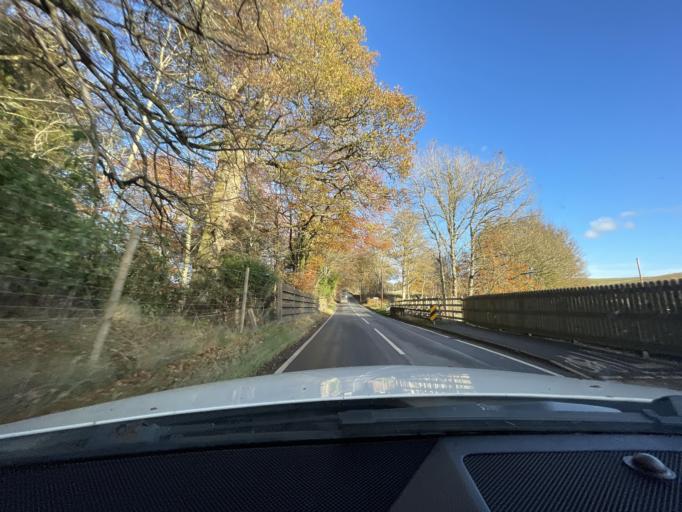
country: GB
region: Scotland
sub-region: Highland
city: Inverness
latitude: 57.4306
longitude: -4.2793
